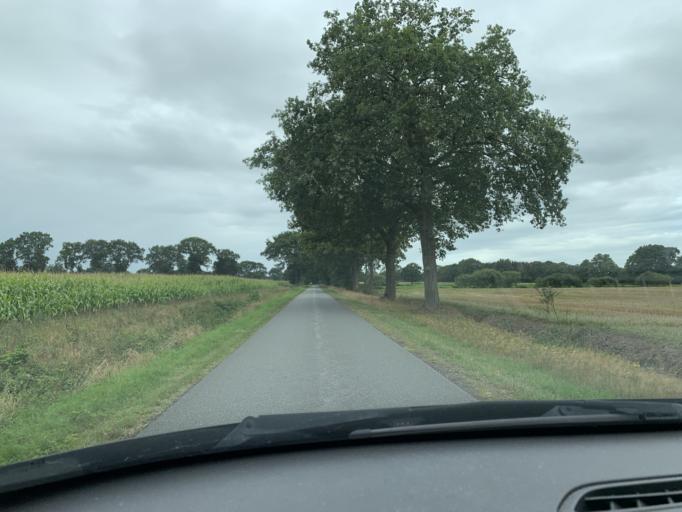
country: DE
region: Lower Saxony
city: Westerstede
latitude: 53.2634
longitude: 7.8871
